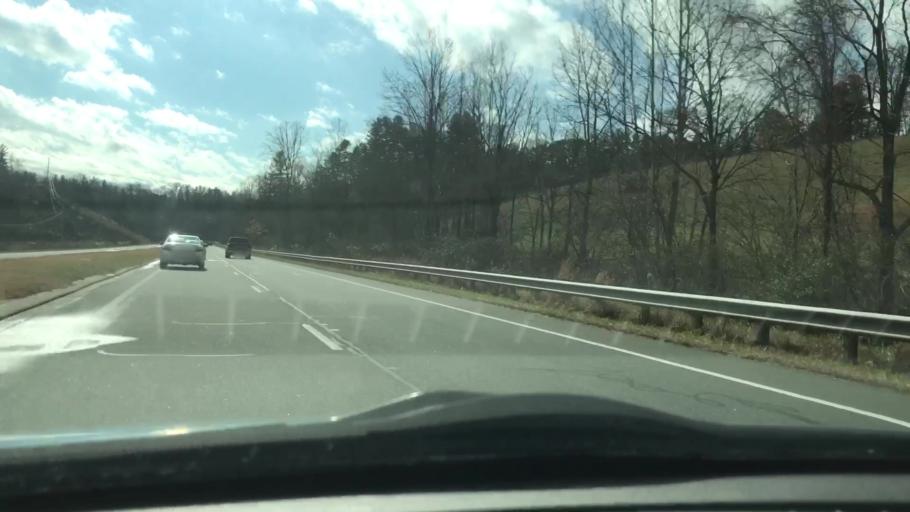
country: US
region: North Carolina
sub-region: Madison County
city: Mars Hill
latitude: 35.8595
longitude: -82.4865
